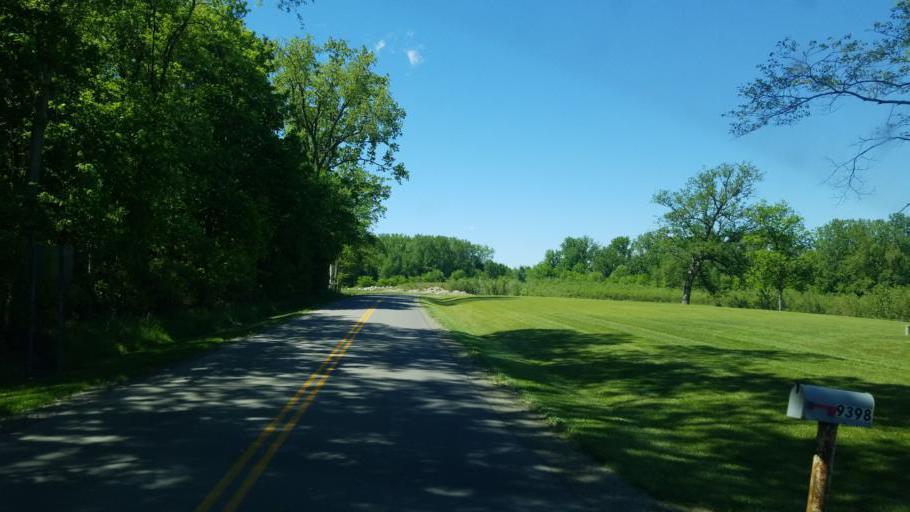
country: US
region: Ohio
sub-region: Logan County
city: Russells Point
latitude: 40.4208
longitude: -83.9223
